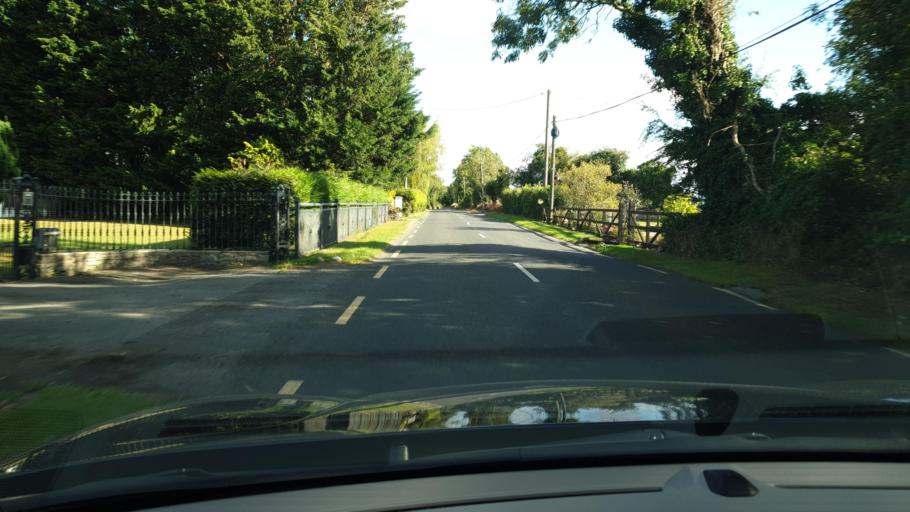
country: IE
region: Leinster
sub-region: An Mhi
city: Ashbourne
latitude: 53.4746
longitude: -6.4242
